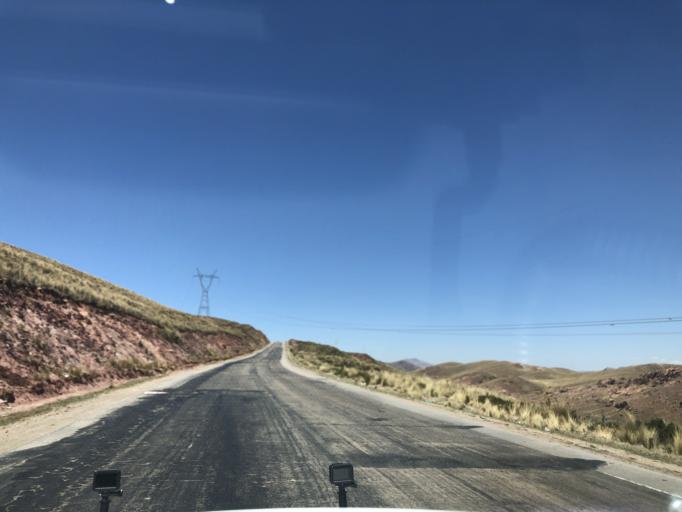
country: BO
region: Cochabamba
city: Colchani
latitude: -17.7000
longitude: -66.6957
